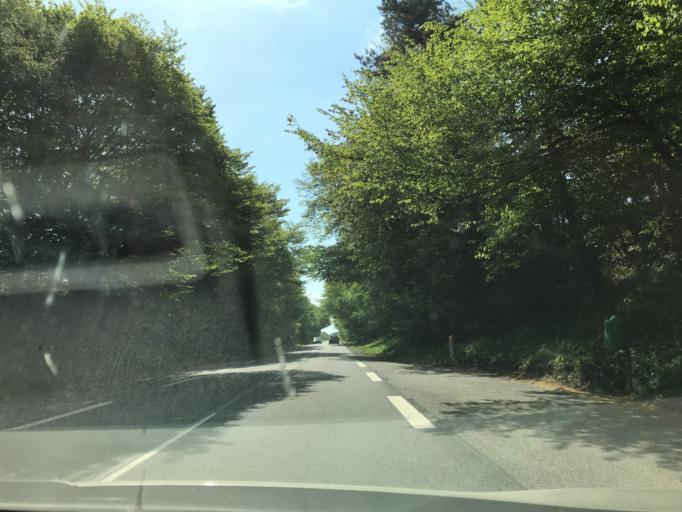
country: DK
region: South Denmark
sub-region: Middelfart Kommune
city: Ejby
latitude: 55.3717
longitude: 9.9219
